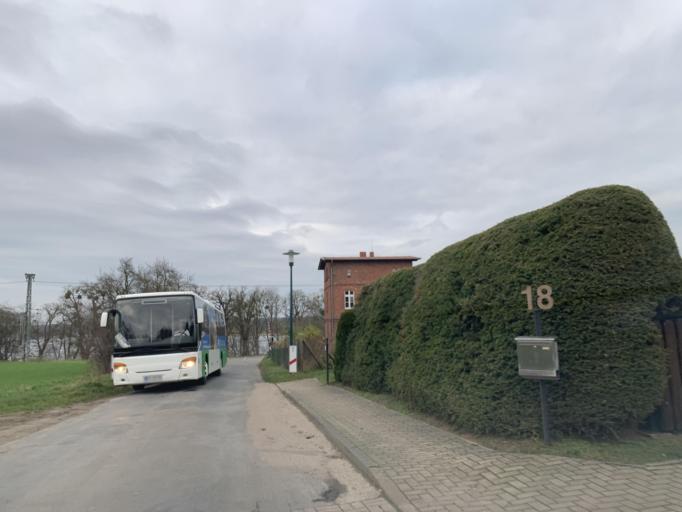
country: DE
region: Mecklenburg-Vorpommern
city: Blankensee
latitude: 53.3973
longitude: 13.2285
